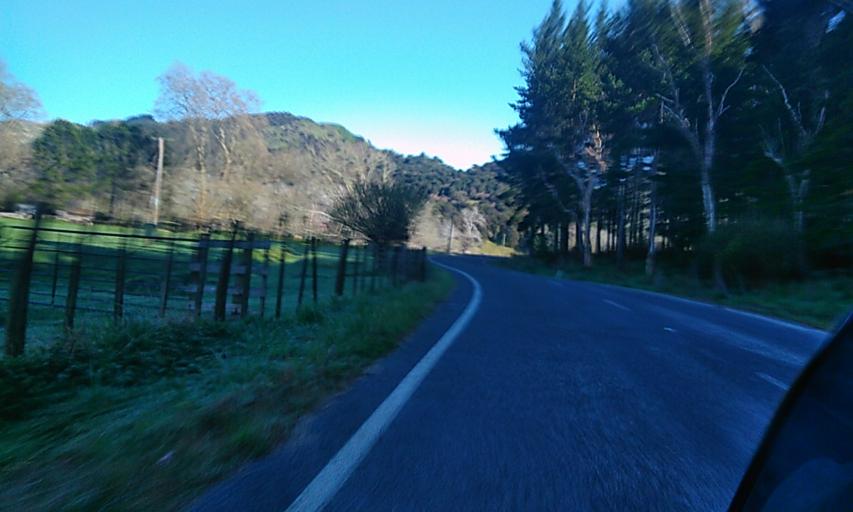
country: NZ
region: Gisborne
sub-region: Gisborne District
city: Gisborne
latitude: -38.5446
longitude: 178.0324
